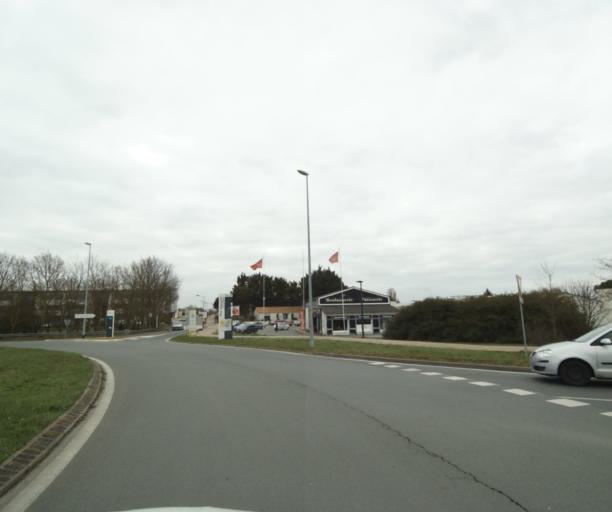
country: FR
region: Poitou-Charentes
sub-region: Departement de la Charente-Maritime
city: Lagord
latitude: 46.1902
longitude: -1.1470
